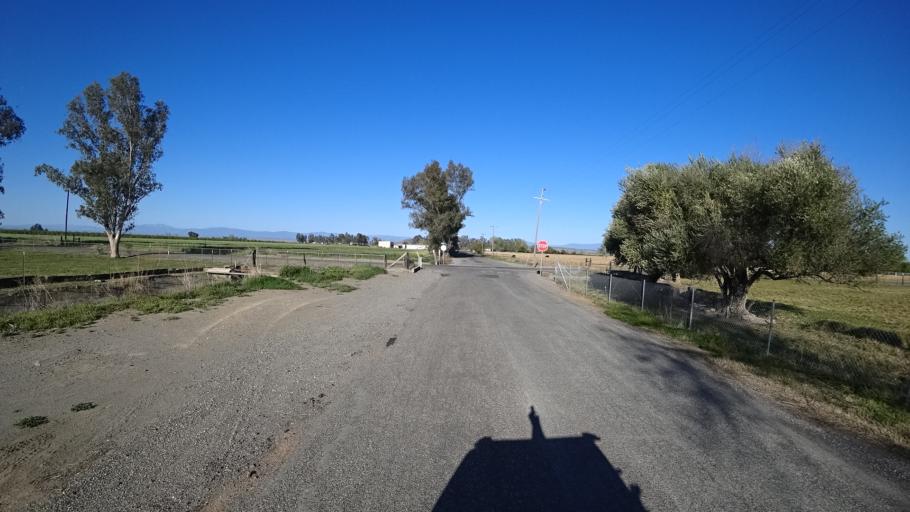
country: US
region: California
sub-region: Glenn County
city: Orland
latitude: 39.7550
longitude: -122.2384
